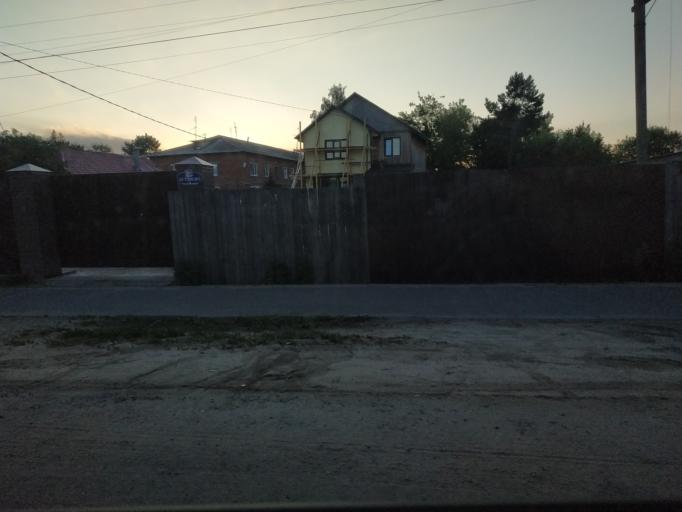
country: RU
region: Moskovskaya
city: Chernogolovka
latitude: 56.0635
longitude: 38.2589
